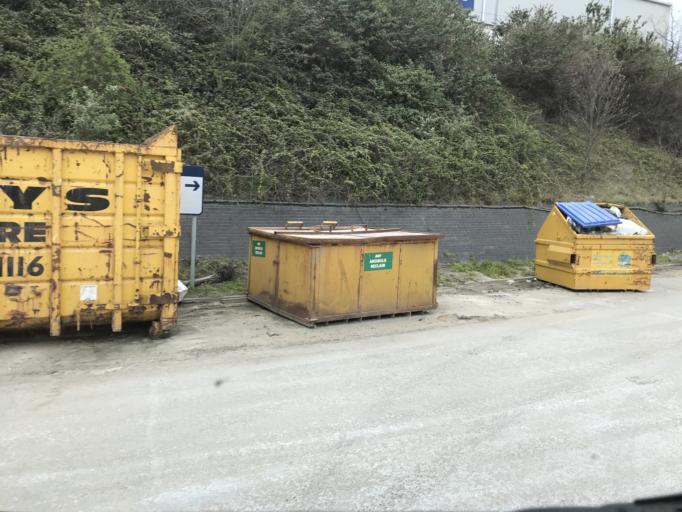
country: GB
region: England
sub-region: Cheshire West and Chester
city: Ellesmere Port
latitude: 53.3501
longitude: -2.9037
